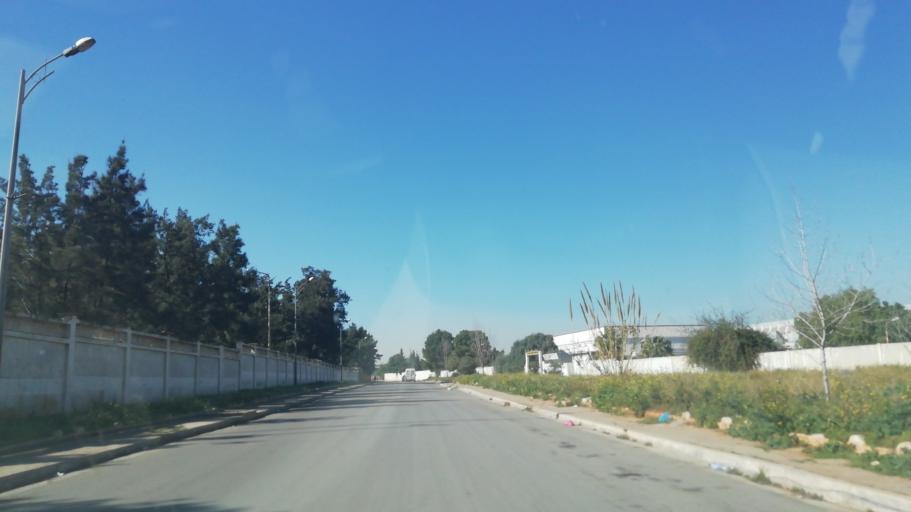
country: DZ
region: Oran
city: Es Senia
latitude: 35.6652
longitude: -0.6251
